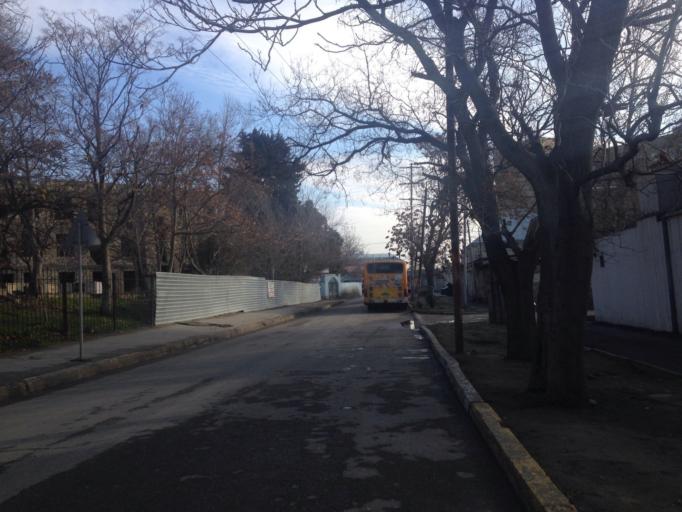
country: AZ
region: Baki
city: Baku
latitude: 40.3933
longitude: 49.8755
